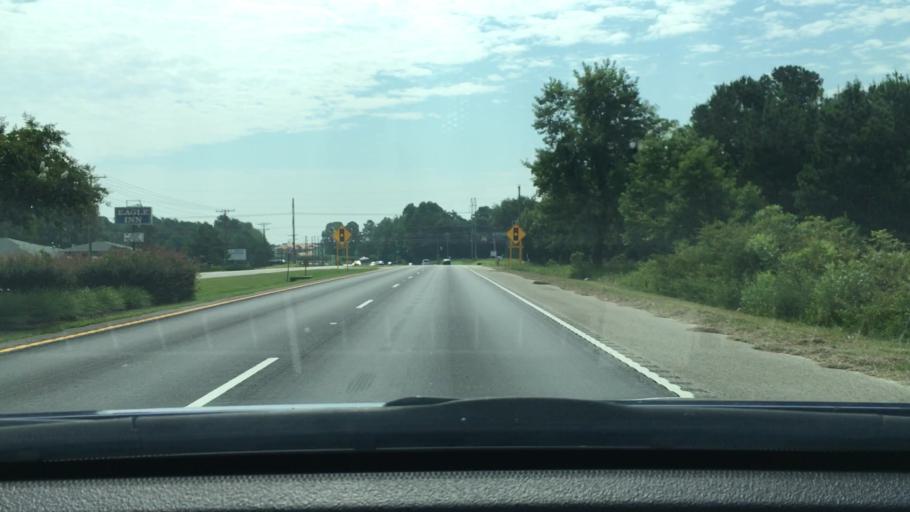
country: US
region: South Carolina
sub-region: Sumter County
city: Cherryvale
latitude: 33.9626
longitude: -80.4313
